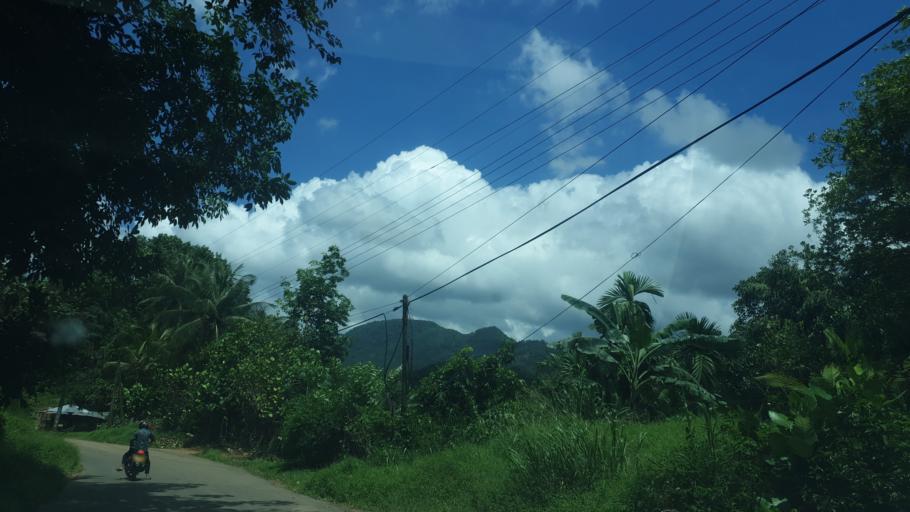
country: LK
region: Sabaragamuwa
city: Ratnapura
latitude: 6.4697
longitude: 80.4257
